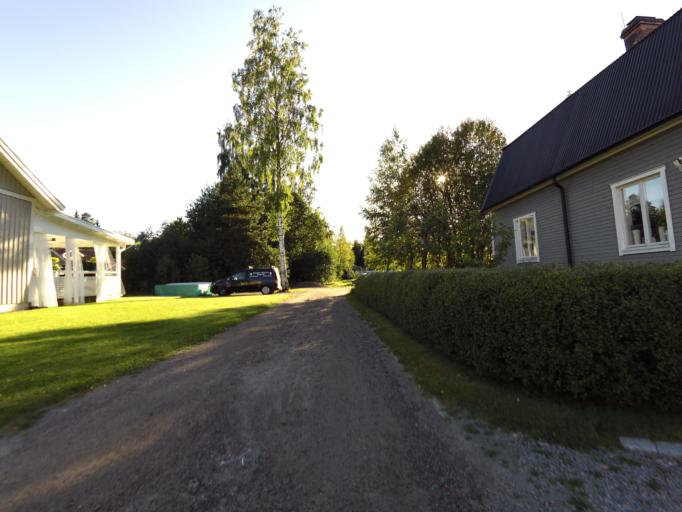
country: SE
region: Gaevleborg
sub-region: Gavle Kommun
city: Gavle
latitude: 60.7096
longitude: 17.1439
